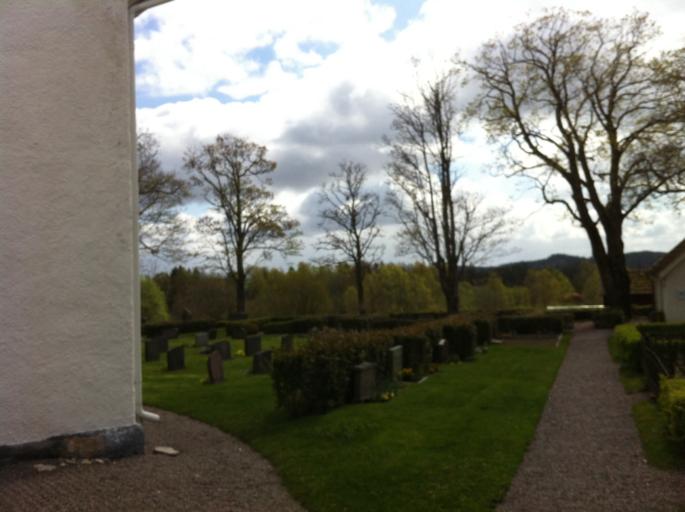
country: SE
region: Vaestra Goetaland
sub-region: Alingsas Kommun
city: Ingared
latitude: 57.8168
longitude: 12.5604
